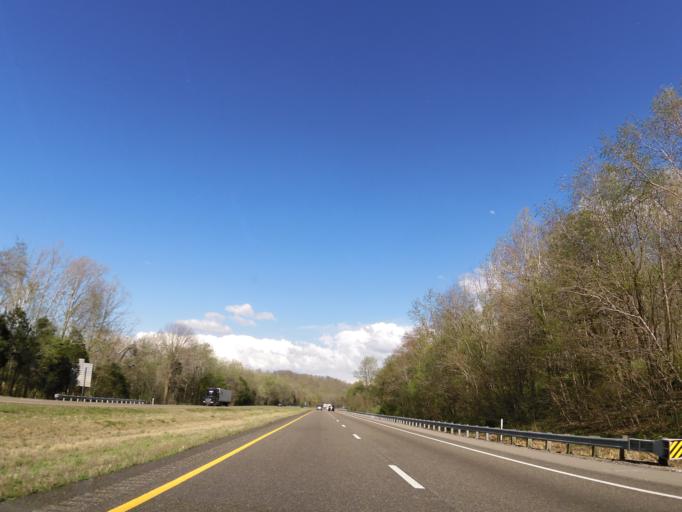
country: US
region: Tennessee
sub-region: Humphreys County
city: New Johnsonville
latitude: 35.8668
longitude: -87.8838
